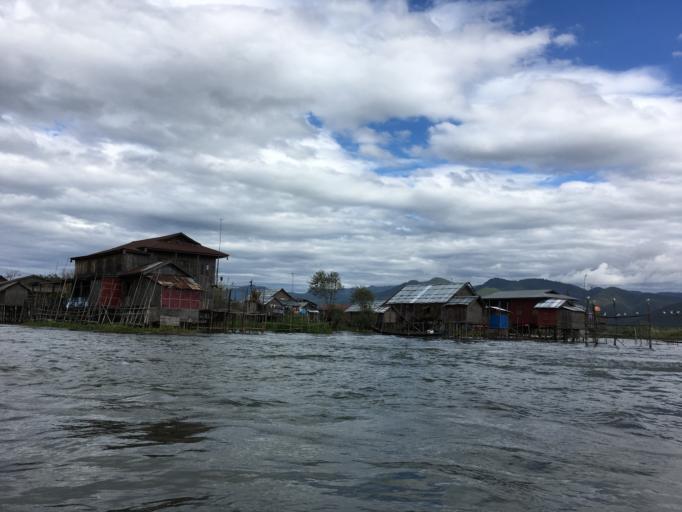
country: MM
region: Shan
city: Taunggyi
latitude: 20.4580
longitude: 96.9069
